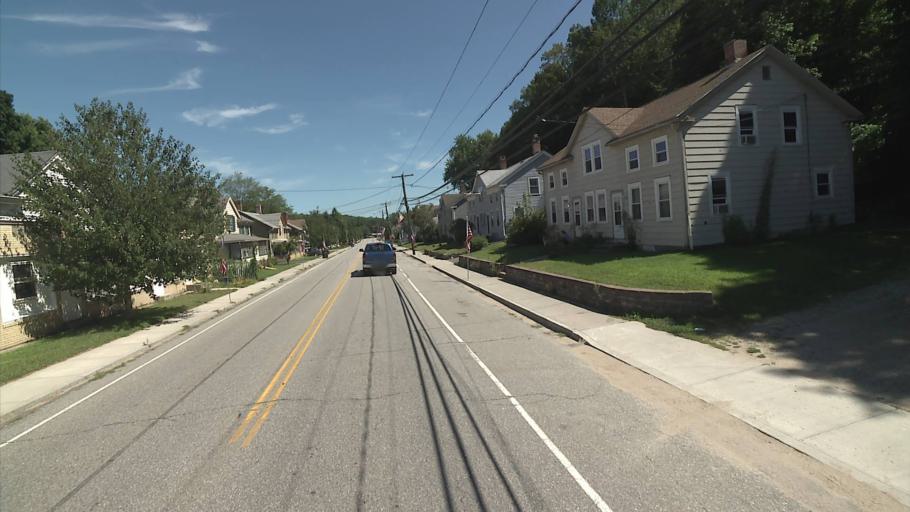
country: US
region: Connecticut
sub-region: New London County
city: Baltic
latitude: 41.6151
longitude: -72.0803
